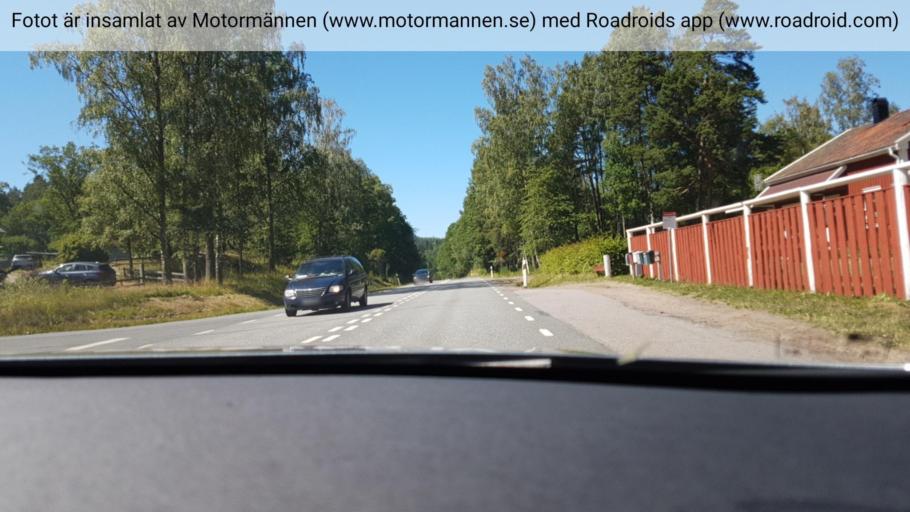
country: SE
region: Joenkoeping
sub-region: Jonkopings Kommun
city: Asa
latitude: 58.0099
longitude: 14.5340
